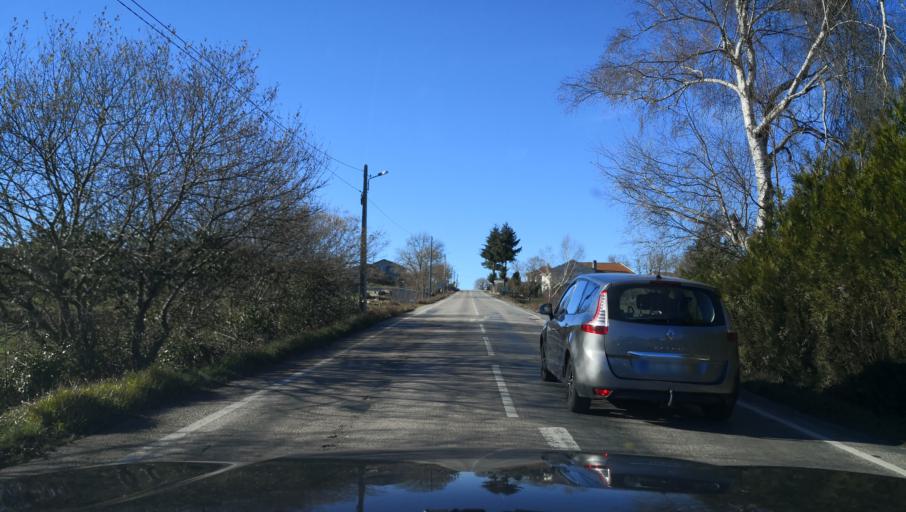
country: PT
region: Vila Real
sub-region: Vila Pouca de Aguiar
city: Vila Pouca de Aguiar
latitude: 41.4999
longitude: -7.6850
